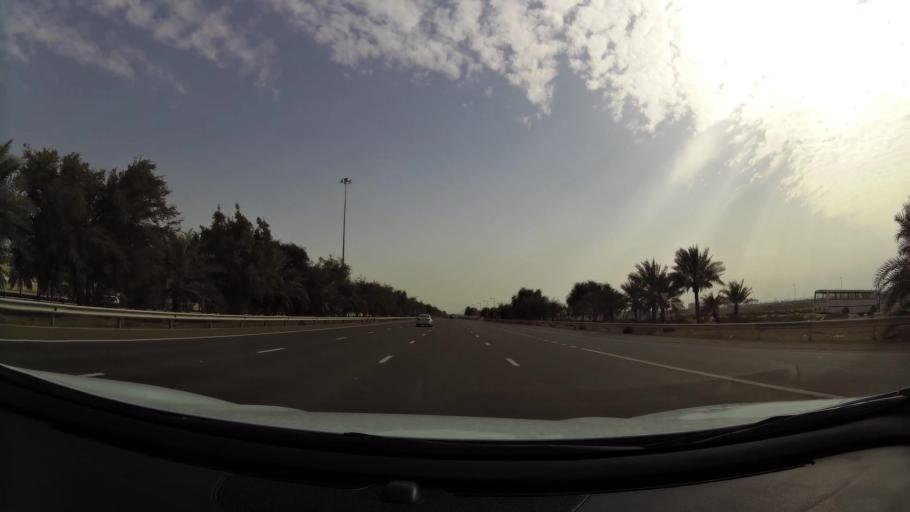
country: AE
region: Abu Dhabi
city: Abu Dhabi
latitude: 24.4415
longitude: 54.6782
